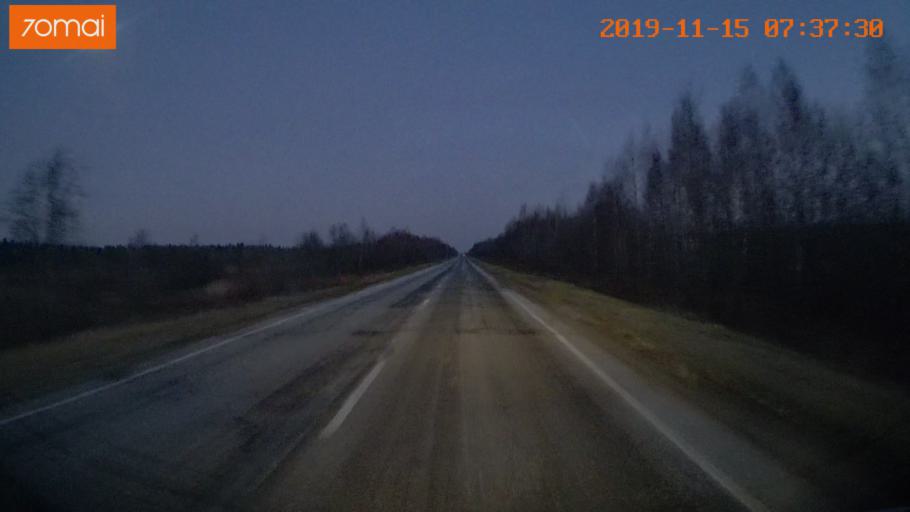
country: RU
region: Vologda
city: Sheksna
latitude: 58.7476
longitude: 38.4196
